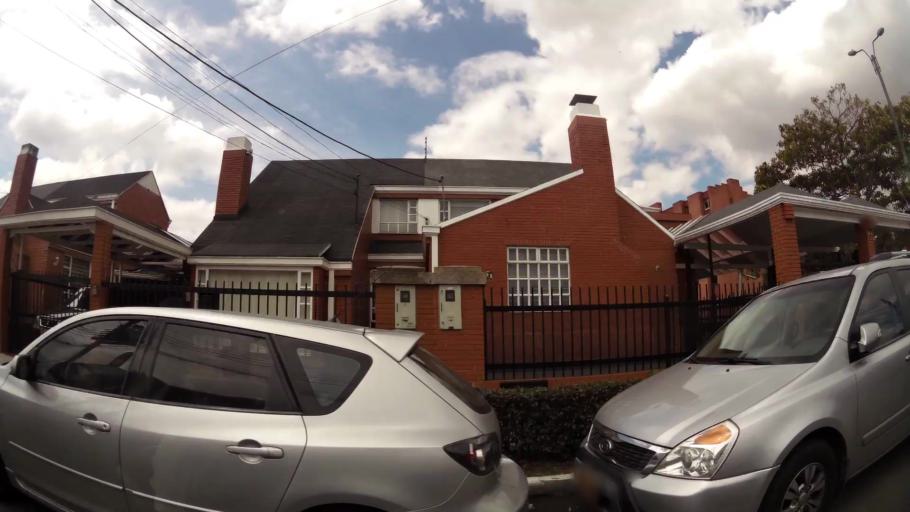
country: CO
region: Bogota D.C.
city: Barrio San Luis
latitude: 4.7051
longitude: -74.0642
